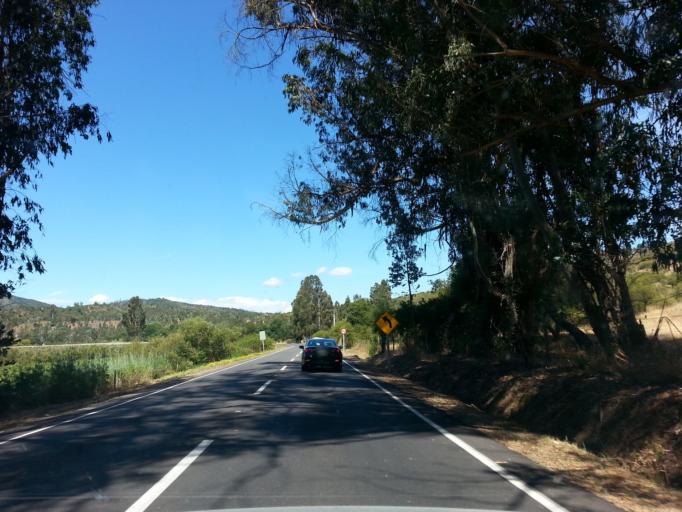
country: CL
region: Valparaiso
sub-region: Provincia de Marga Marga
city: Quilpue
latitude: -33.2258
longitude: -71.3988
